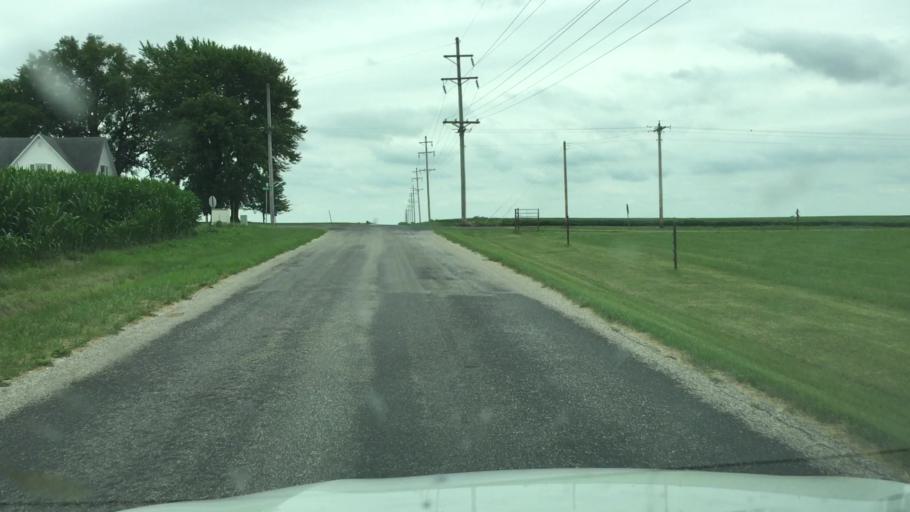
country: US
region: Illinois
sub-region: Hancock County
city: Carthage
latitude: 40.4013
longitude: -91.0825
